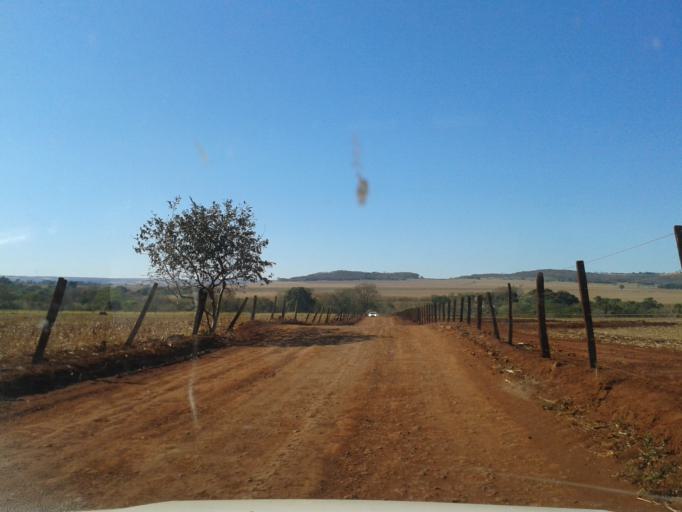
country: BR
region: Minas Gerais
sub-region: Centralina
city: Centralina
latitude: -18.5870
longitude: -49.1836
